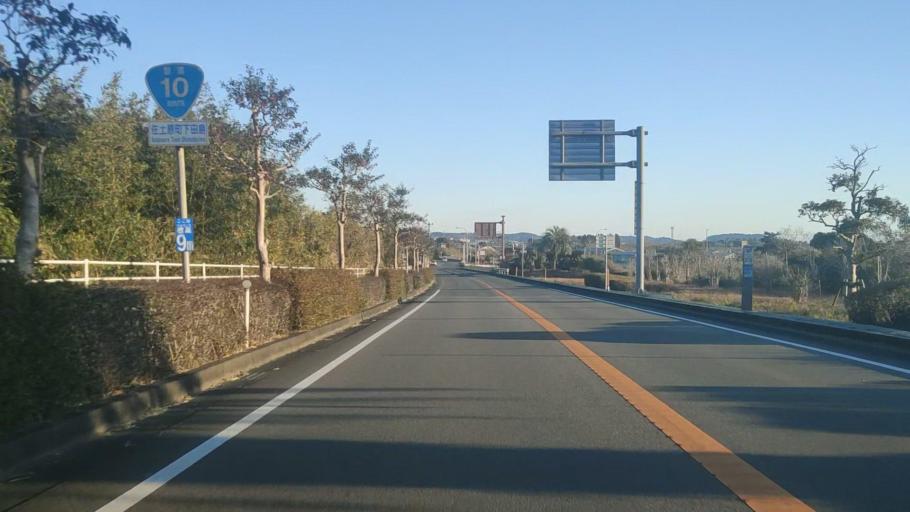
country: JP
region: Miyazaki
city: Tsuma
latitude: 32.0398
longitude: 131.4684
